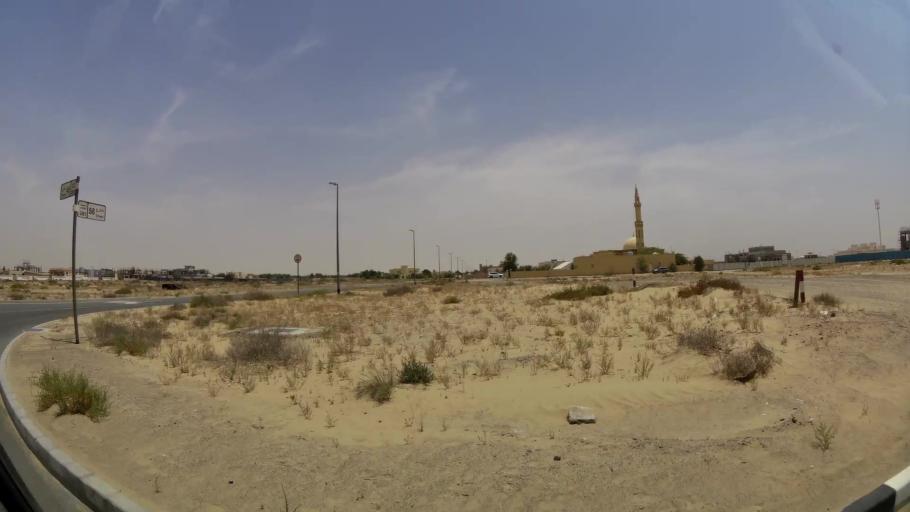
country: AE
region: Ash Shariqah
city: Sharjah
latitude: 25.2485
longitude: 55.4751
